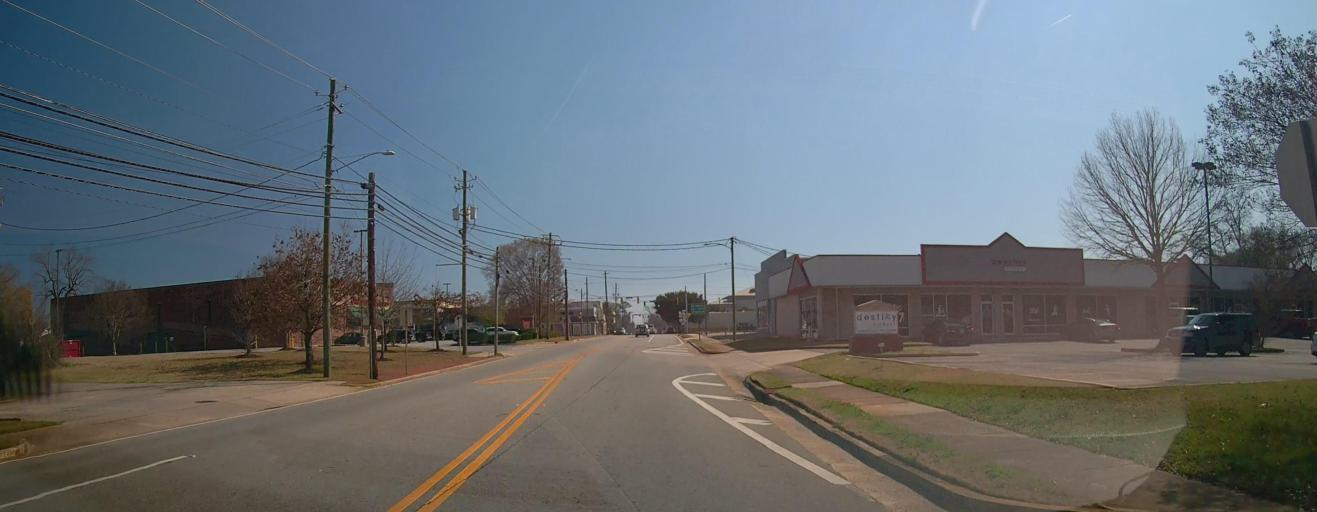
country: US
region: Georgia
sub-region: Houston County
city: Perry
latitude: 32.4602
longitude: -83.7345
